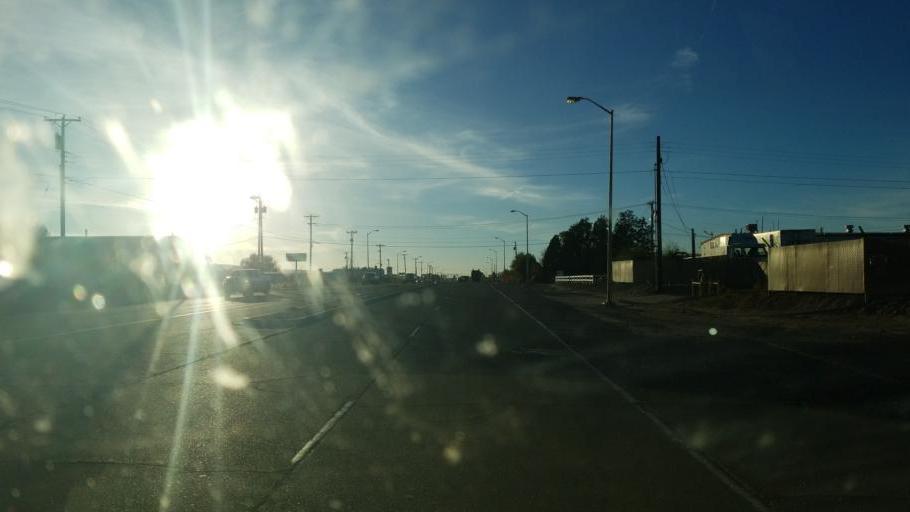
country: US
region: New Mexico
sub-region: San Juan County
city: Farmington
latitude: 36.7191
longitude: -108.1714
